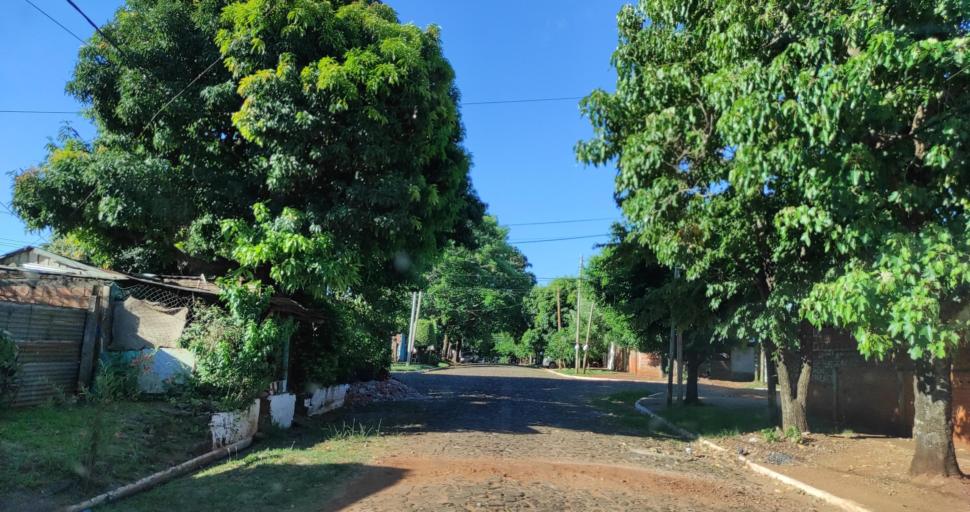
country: AR
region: Misiones
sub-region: Departamento de Capital
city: Posadas
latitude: -27.3794
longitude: -55.9240
